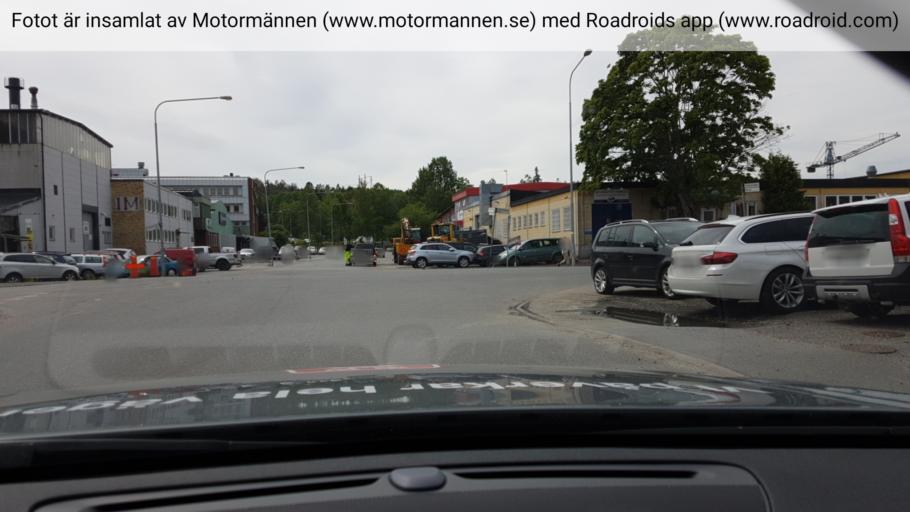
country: SE
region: Stockholm
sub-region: Huddinge Kommun
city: Huddinge
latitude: 59.2301
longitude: 17.9942
